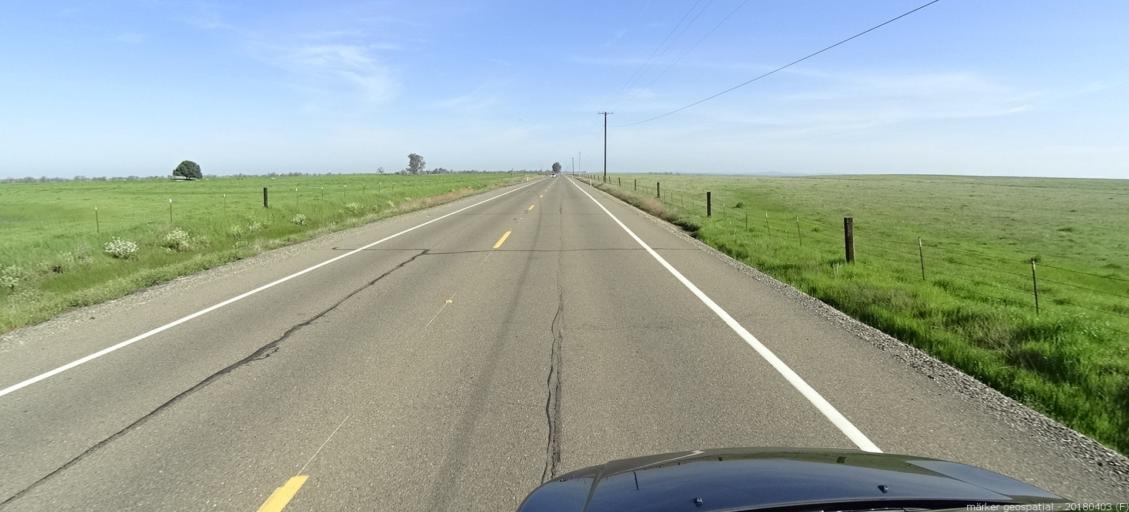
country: US
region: California
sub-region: Sacramento County
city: Clay
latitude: 38.3579
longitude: -121.1684
